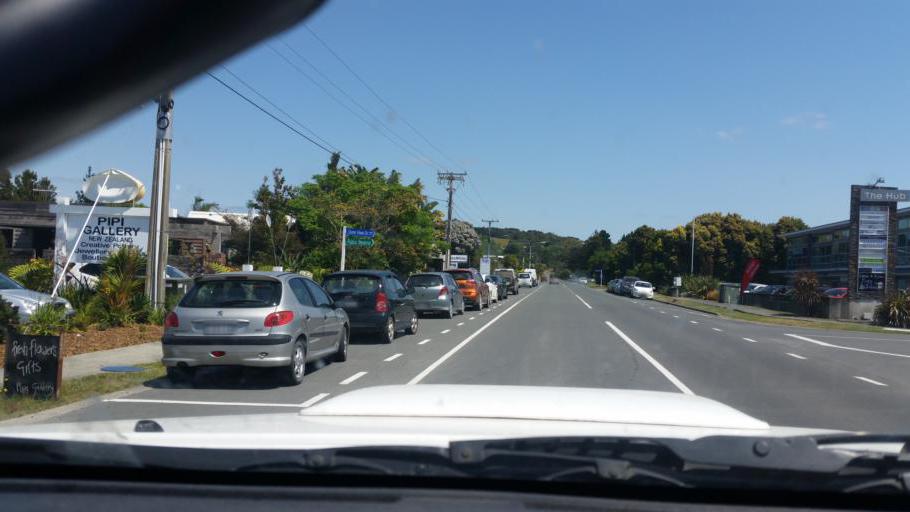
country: NZ
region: Auckland
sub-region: Auckland
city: Wellsford
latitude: -36.1252
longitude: 174.5753
